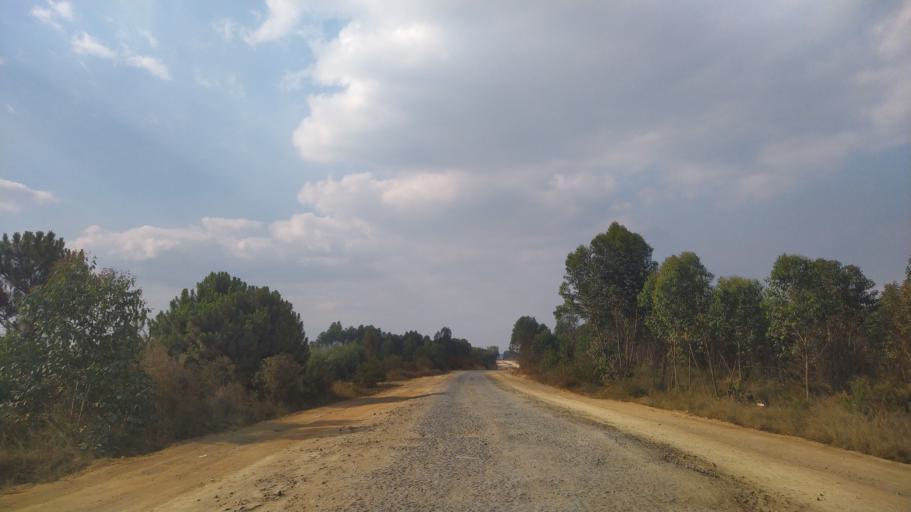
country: MG
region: Alaotra Mangoro
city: Moramanga
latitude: -18.6427
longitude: 48.2755
